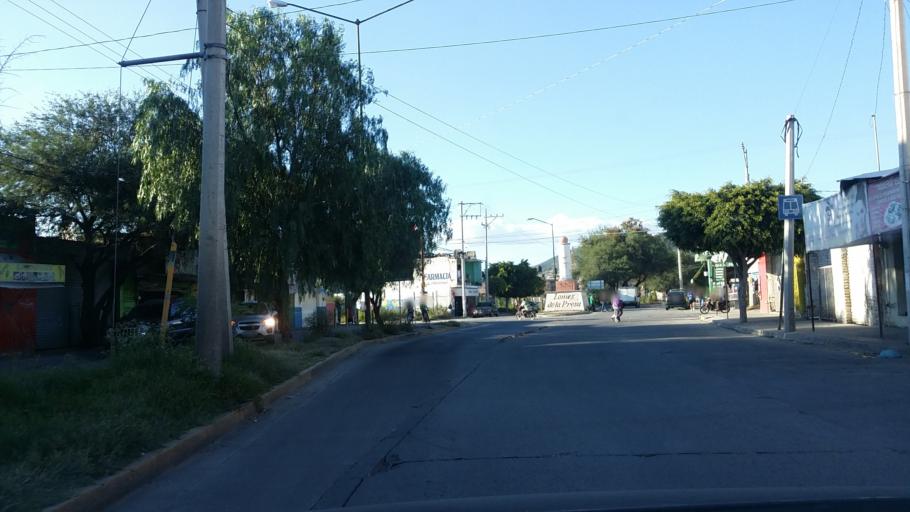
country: MX
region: Guanajuato
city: Leon
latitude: 21.1870
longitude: -101.6758
